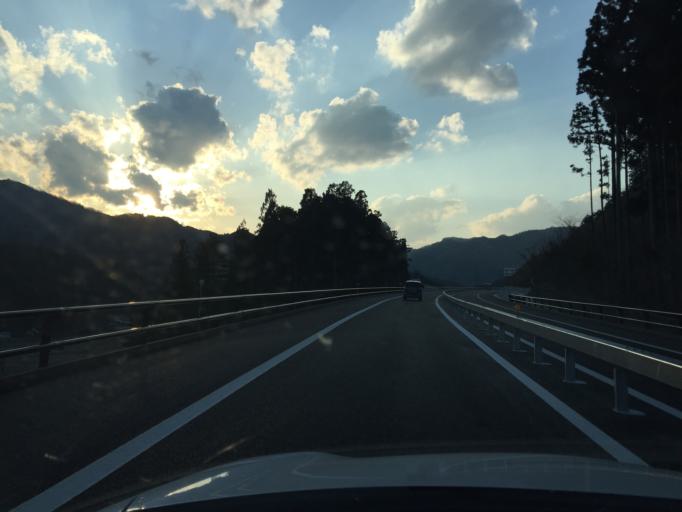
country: JP
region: Miyagi
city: Marumori
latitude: 37.7750
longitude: 140.8369
